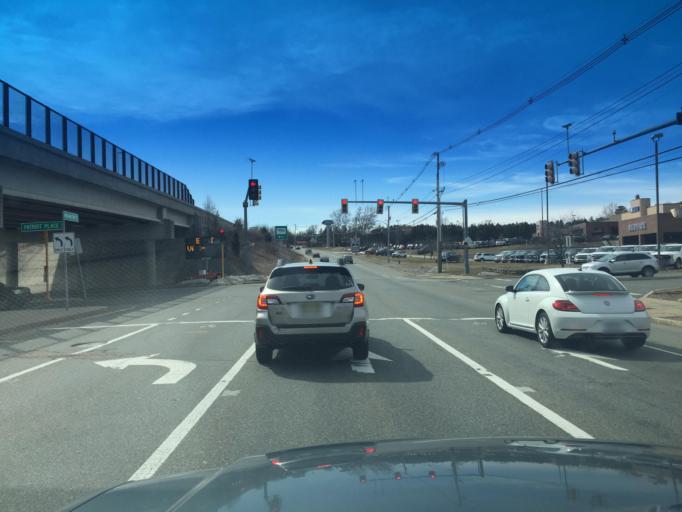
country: US
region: Massachusetts
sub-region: Norfolk County
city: Foxborough
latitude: 42.0976
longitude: -71.2650
